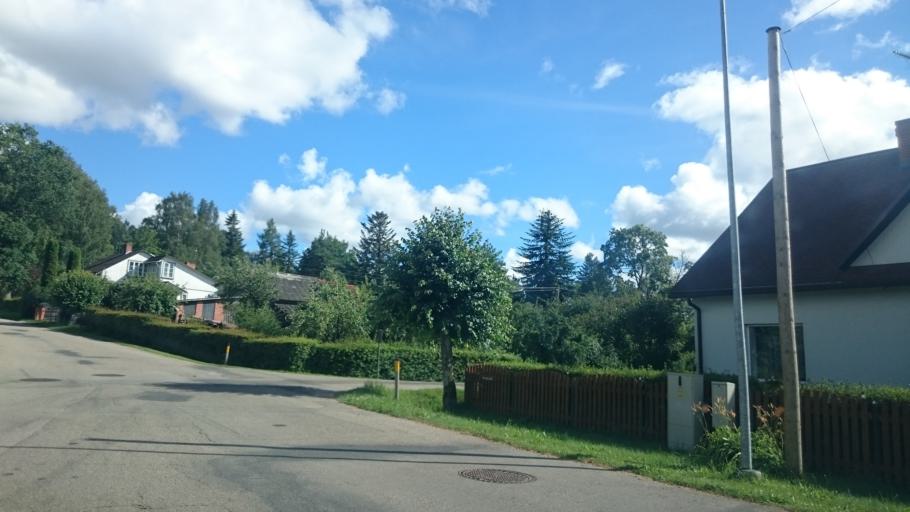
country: LV
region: Aizpute
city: Aizpute
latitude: 56.7178
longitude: 21.5938
